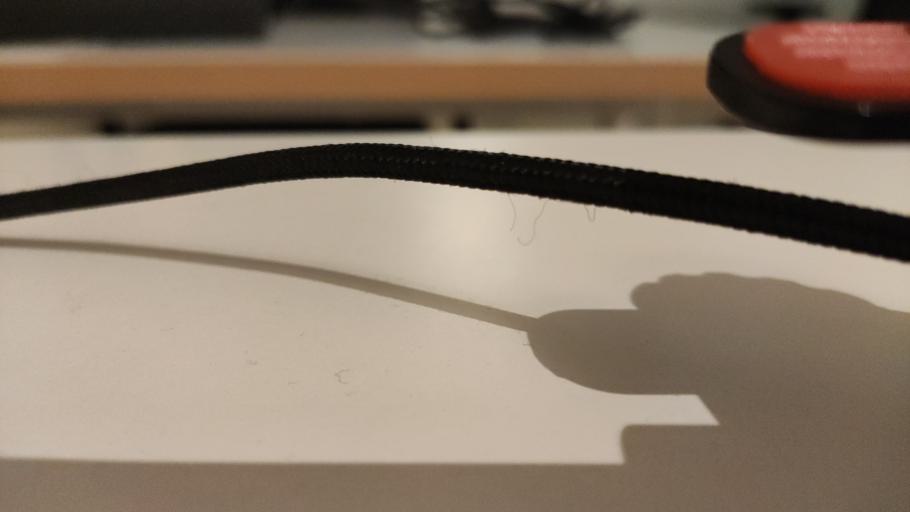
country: RU
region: Moskovskaya
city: Likino-Dulevo
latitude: 55.7006
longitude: 38.9570
